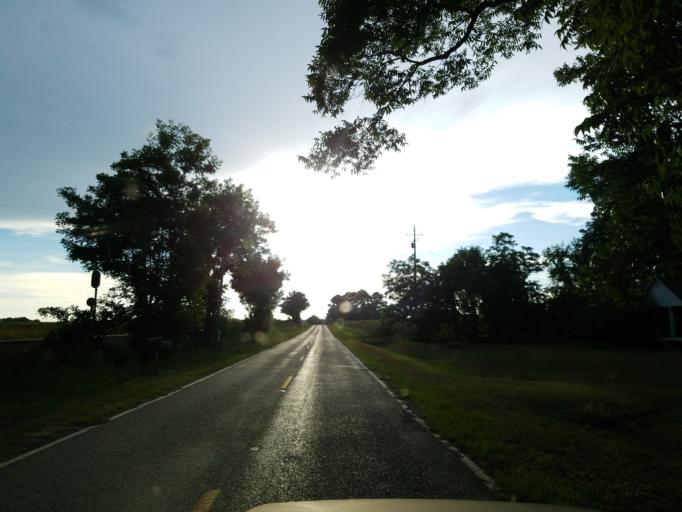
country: US
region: Georgia
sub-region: Tift County
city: Tifton
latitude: 31.5512
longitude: -83.5559
